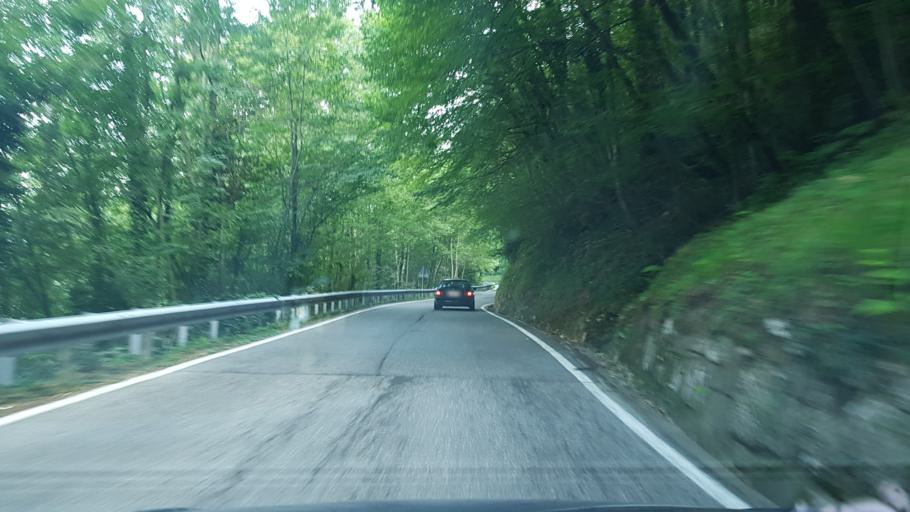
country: IT
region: Veneto
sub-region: Provincia di Vicenza
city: Valli del Pasubio
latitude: 45.7580
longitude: 11.2113
